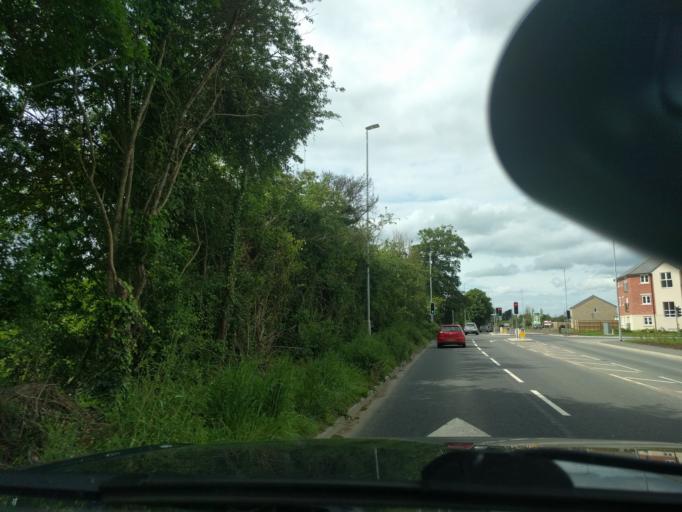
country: GB
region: England
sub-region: Wiltshire
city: Melksham
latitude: 51.3828
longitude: -2.1517
